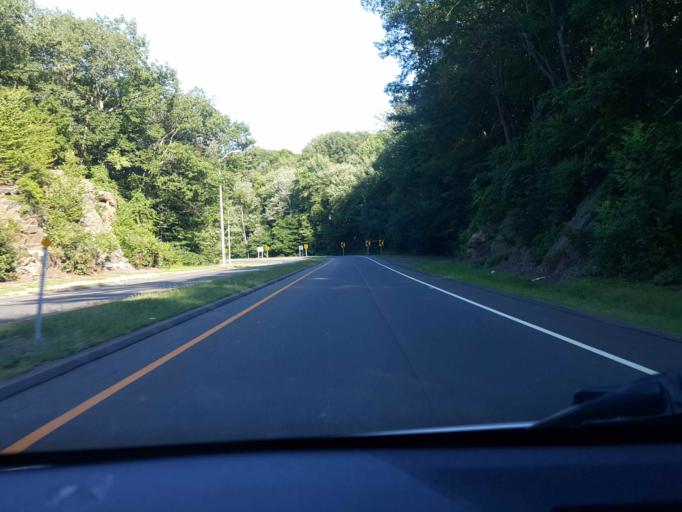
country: US
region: Connecticut
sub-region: New Haven County
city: Guilford
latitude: 41.2955
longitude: -72.7052
